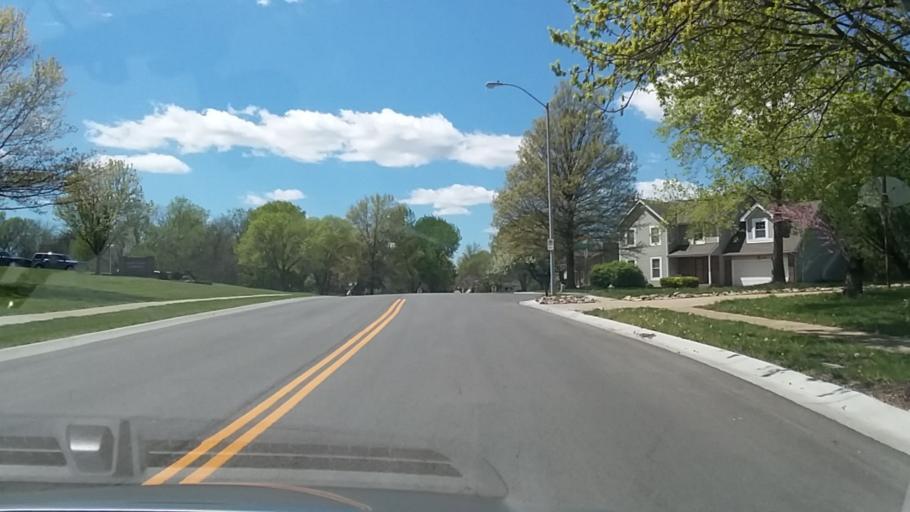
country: US
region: Kansas
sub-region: Johnson County
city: Olathe
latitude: 38.8915
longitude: -94.8605
